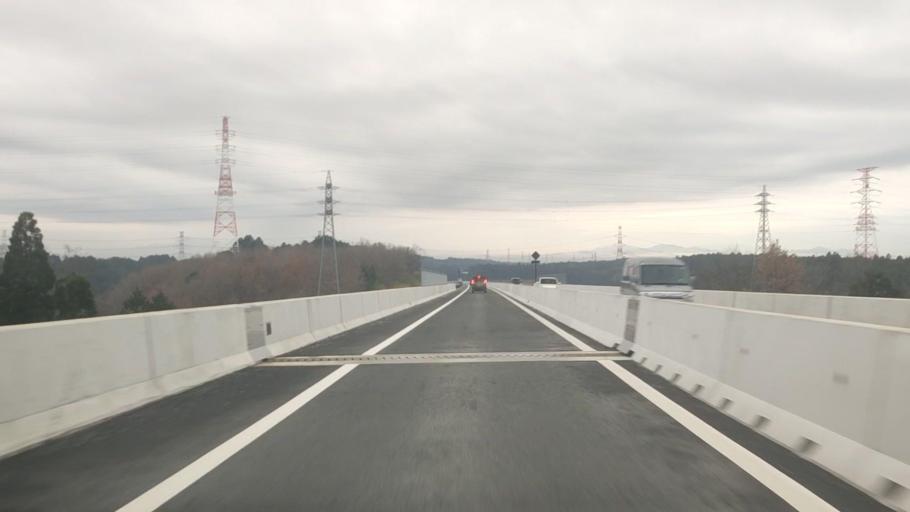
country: JP
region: Kumamoto
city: Ozu
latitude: 32.8999
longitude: 130.9154
